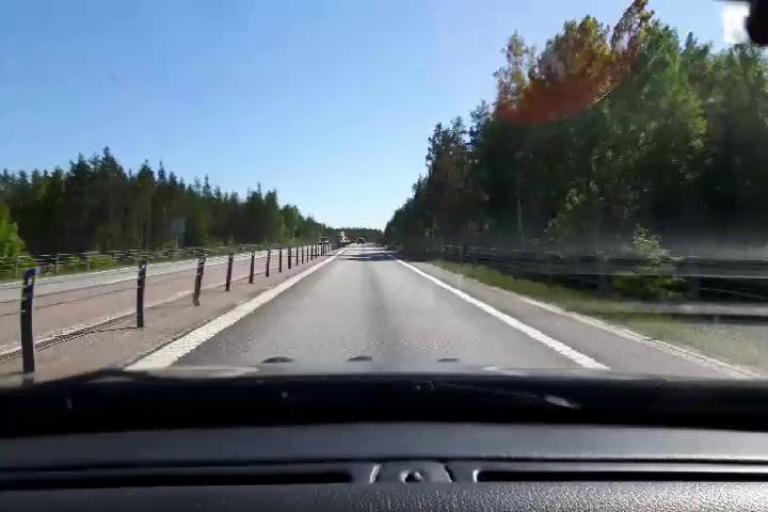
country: SE
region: Gaevleborg
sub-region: Soderhamns Kommun
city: Ljusne
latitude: 61.1203
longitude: 17.0140
